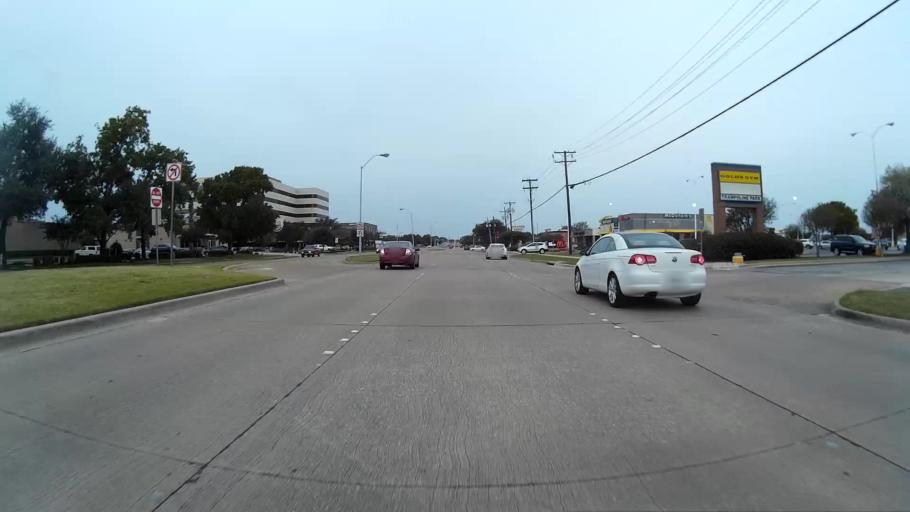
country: US
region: Texas
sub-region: Dallas County
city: Richardson
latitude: 32.9755
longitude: -96.7183
